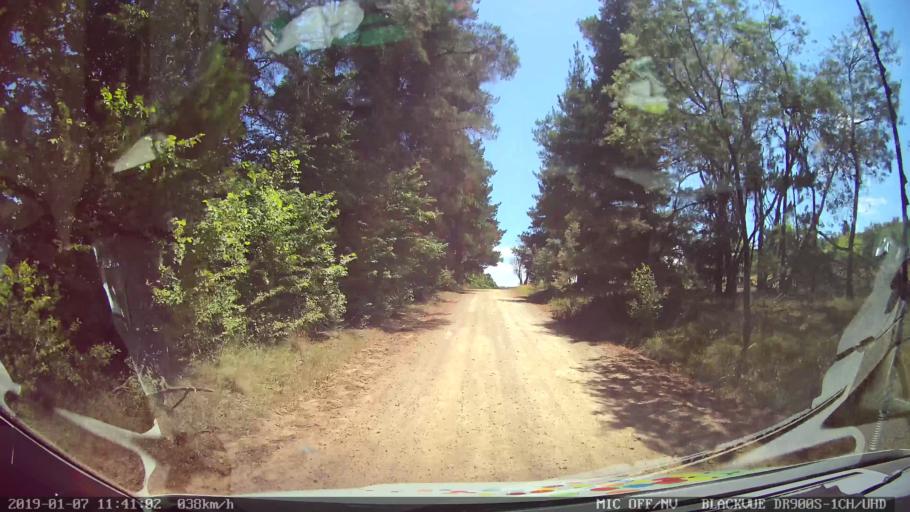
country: AU
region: New South Wales
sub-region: Armidale Dumaresq
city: Armidale
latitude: -30.3622
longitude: 151.5873
